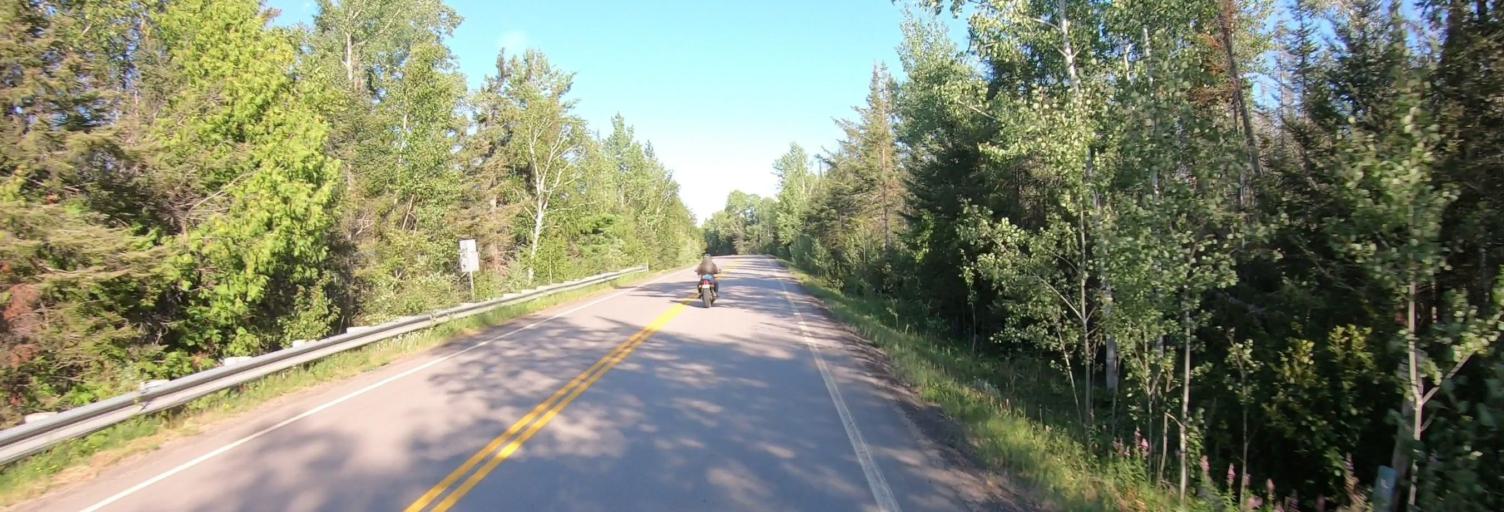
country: US
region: Minnesota
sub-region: Saint Louis County
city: Ely
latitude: 47.9601
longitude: -91.5210
